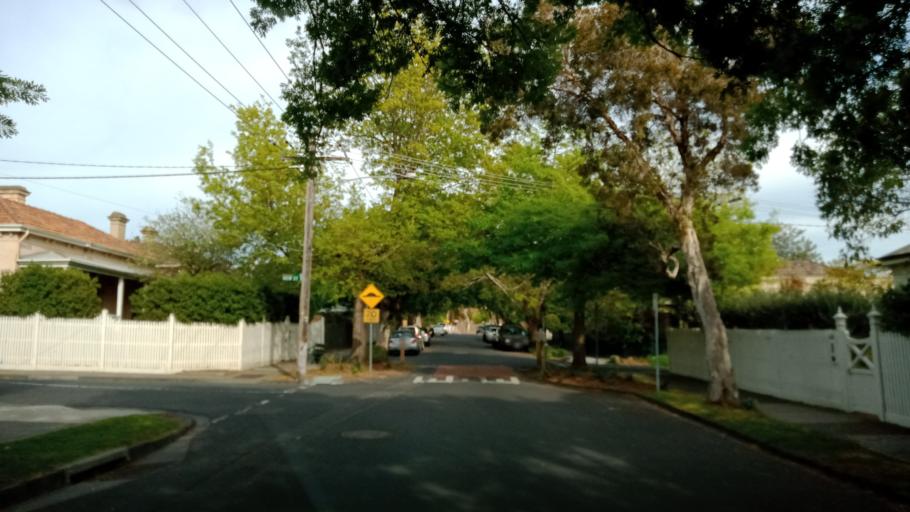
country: AU
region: Victoria
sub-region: Boroondara
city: Hawthorn East
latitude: -37.8236
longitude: 145.0307
